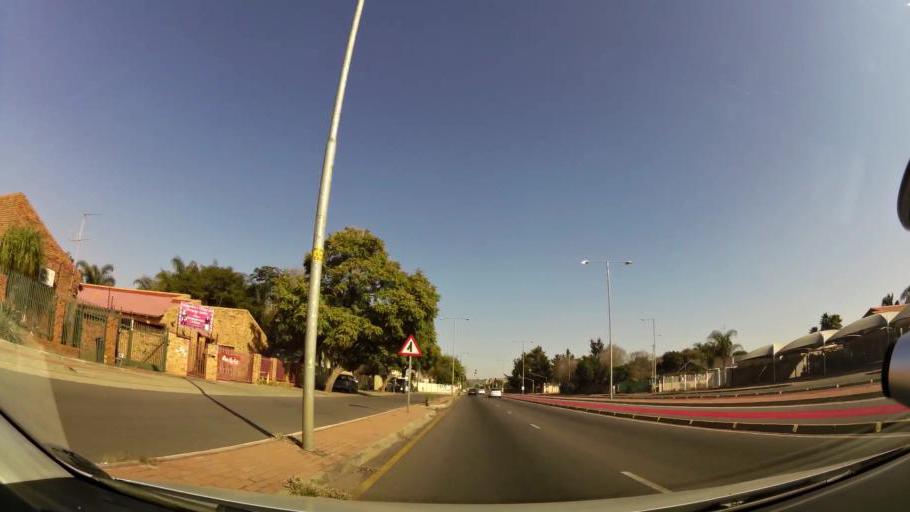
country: ZA
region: Gauteng
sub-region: City of Tshwane Metropolitan Municipality
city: Pretoria
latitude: -25.7041
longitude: 28.1872
